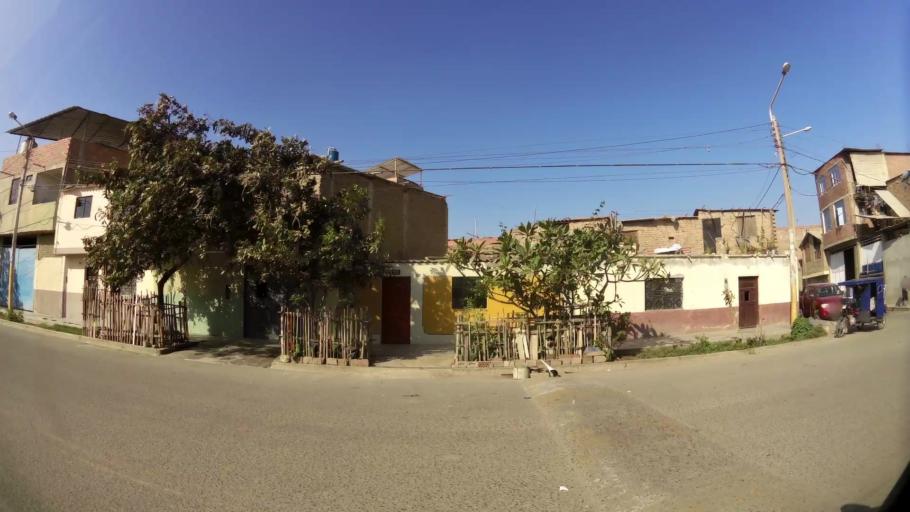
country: PE
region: Lambayeque
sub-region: Provincia de Chiclayo
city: Chiclayo
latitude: -6.7655
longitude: -79.8458
